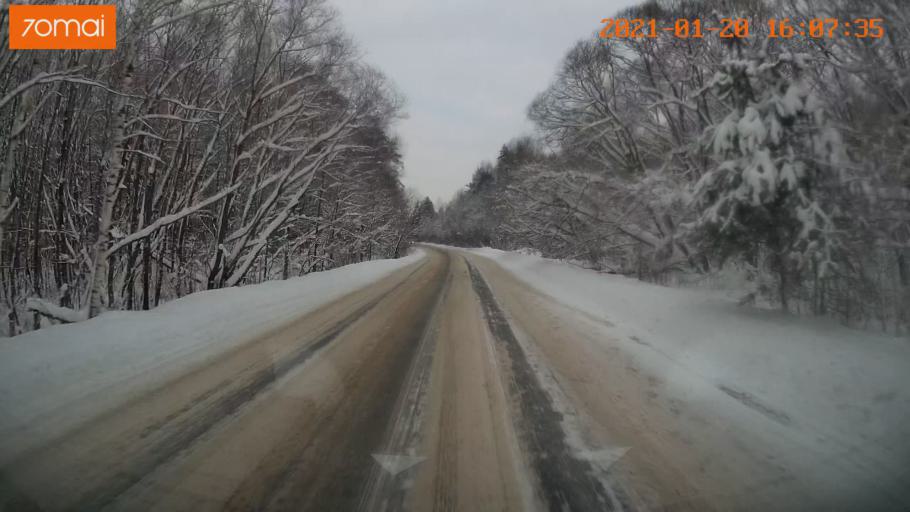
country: RU
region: Vladimir
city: Sudogda
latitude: 56.0745
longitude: 40.7785
